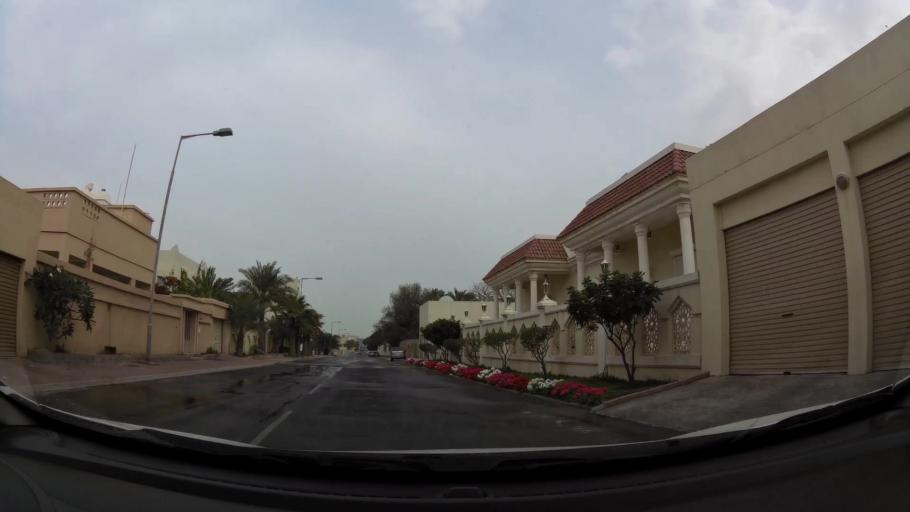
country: BH
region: Northern
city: Ar Rifa'
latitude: 26.1325
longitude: 50.5454
